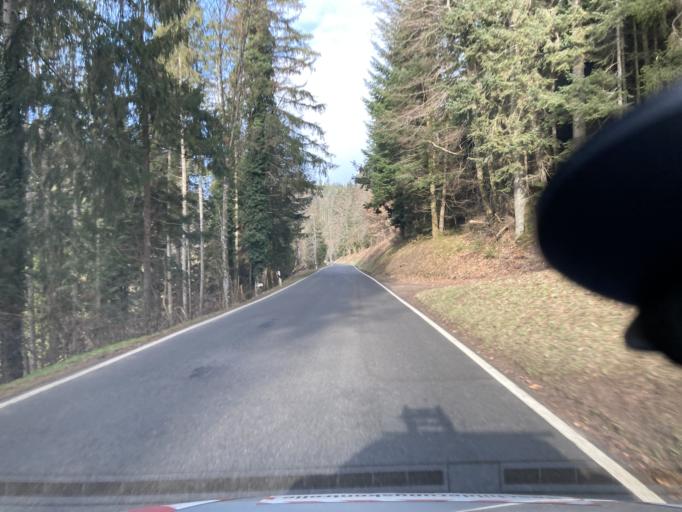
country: DE
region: Baden-Wuerttemberg
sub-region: Karlsruhe Region
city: Bad Teinach-Zavelstein
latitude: 48.6792
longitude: 8.6501
